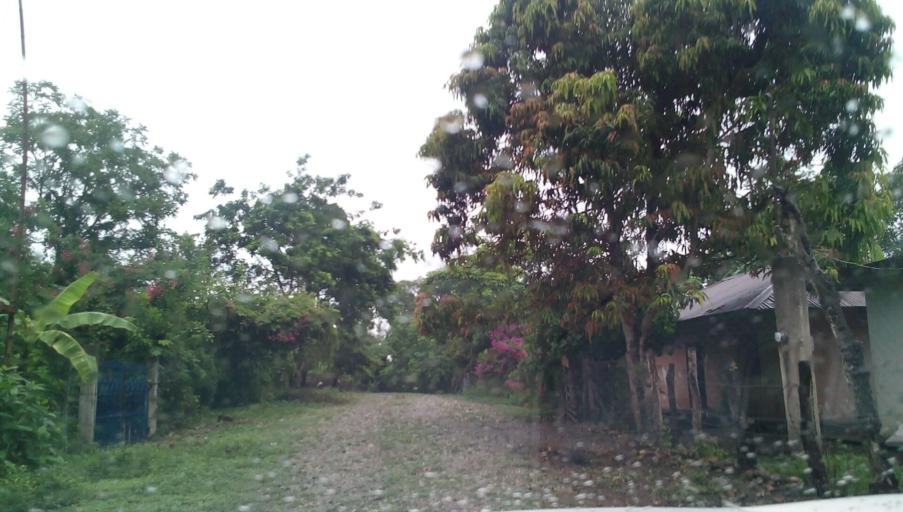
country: MX
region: Veracruz
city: Tempoal de Sanchez
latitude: 21.4138
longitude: -98.4248
